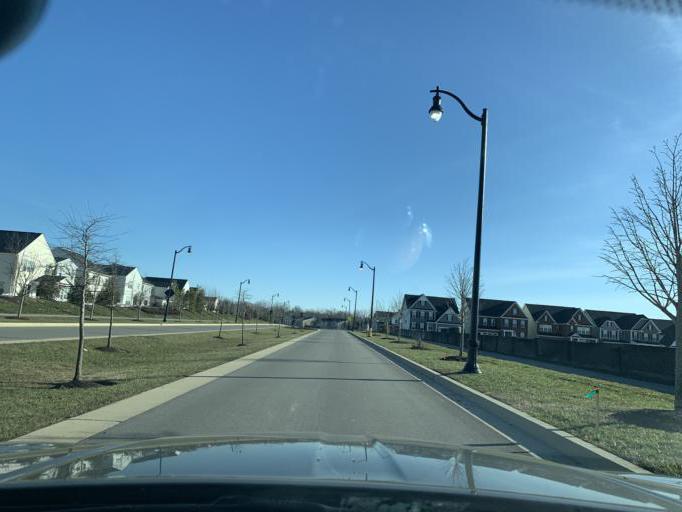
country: US
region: Maryland
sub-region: Anne Arundel County
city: Crofton
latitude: 39.0214
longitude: -76.7237
